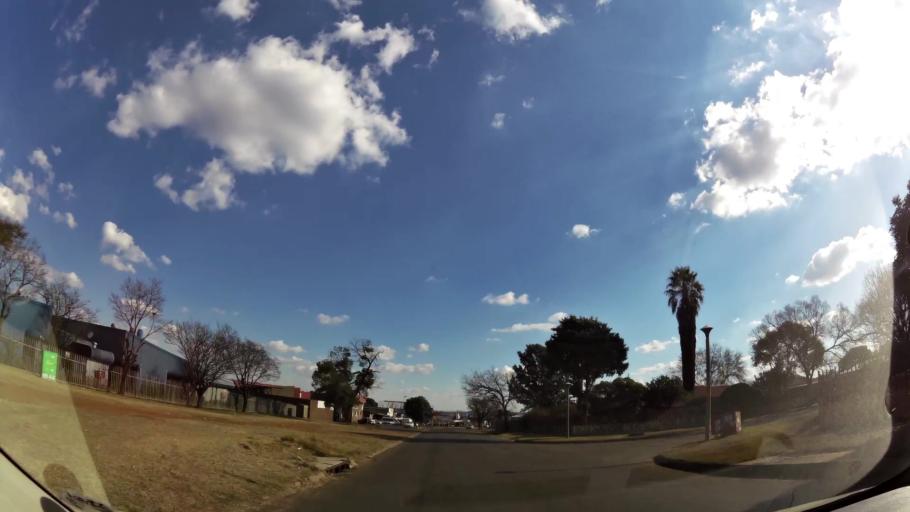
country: ZA
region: Mpumalanga
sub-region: Nkangala District Municipality
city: Witbank
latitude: -25.9019
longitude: 29.2261
